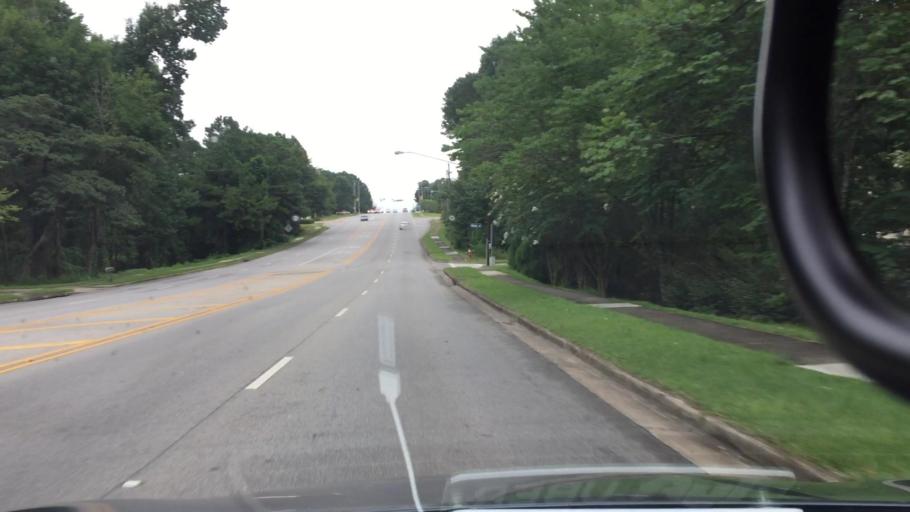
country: US
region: Alabama
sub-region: Lee County
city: Auburn
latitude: 32.6088
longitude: -85.4517
